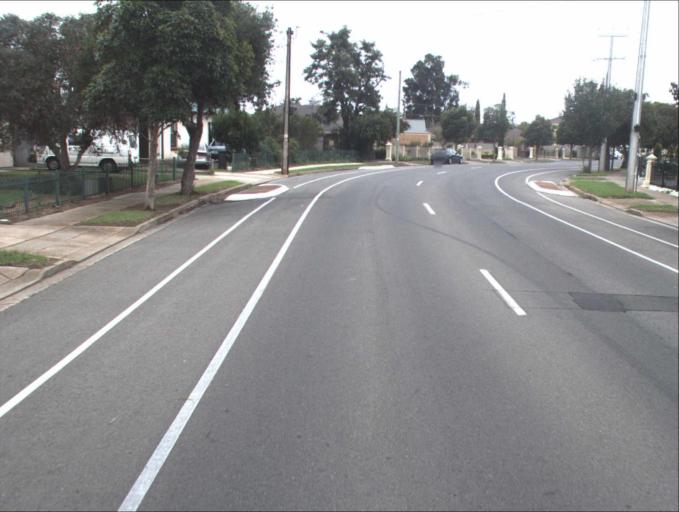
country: AU
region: South Australia
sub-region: Charles Sturt
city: Woodville North
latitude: -34.8673
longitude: 138.5584
